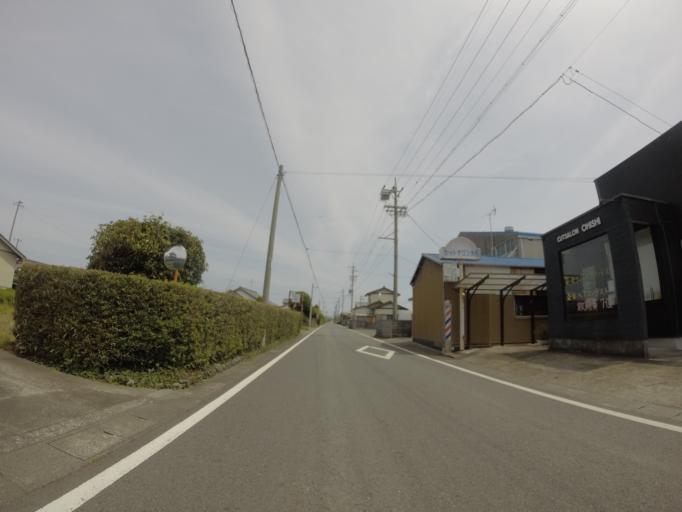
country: JP
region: Shizuoka
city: Yaizu
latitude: 34.7924
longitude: 138.3058
